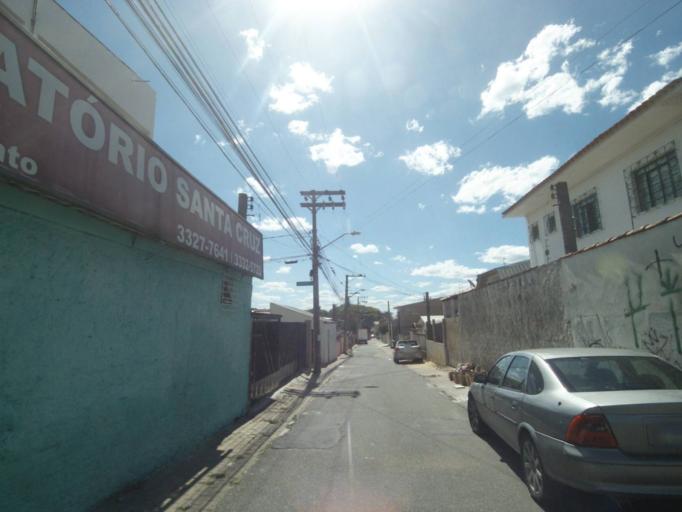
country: BR
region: Parana
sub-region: Curitiba
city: Curitiba
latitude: -25.5083
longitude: -49.3226
